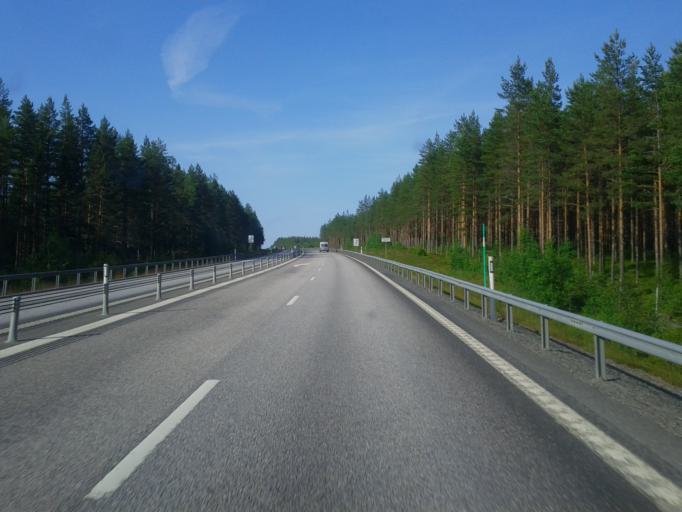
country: SE
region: Vaesterbotten
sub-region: Umea Kommun
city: Saevar
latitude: 63.9313
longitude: 20.6391
